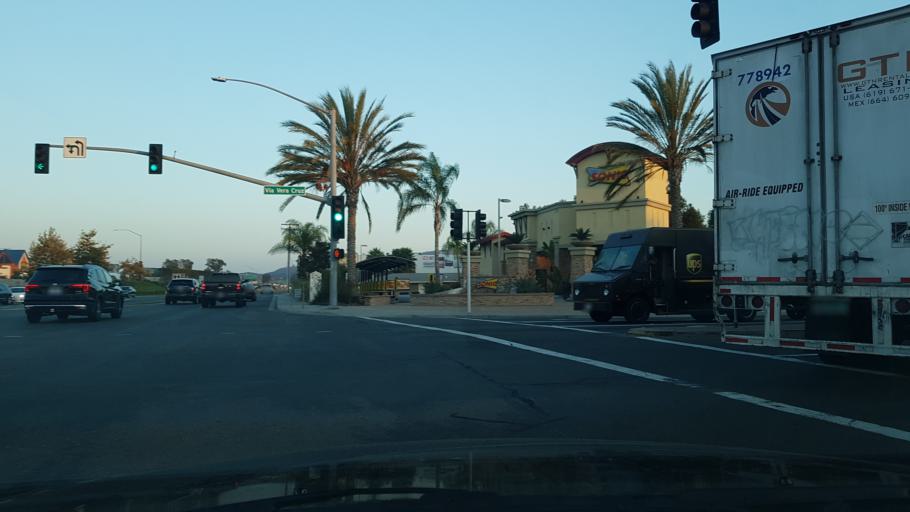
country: US
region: California
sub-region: San Diego County
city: Lake San Marcos
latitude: 33.1426
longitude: -117.1911
